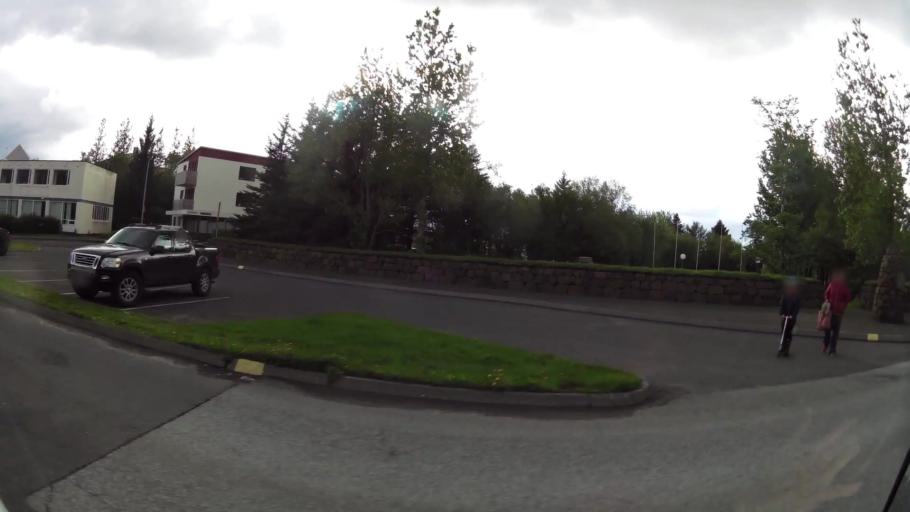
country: IS
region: West
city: Borgarnes
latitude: 64.5393
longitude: -21.9199
